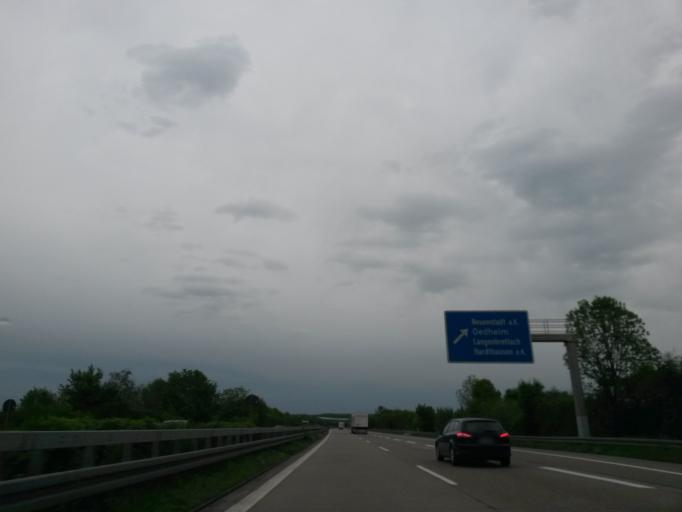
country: DE
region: Baden-Wuerttemberg
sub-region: Regierungsbezirk Stuttgart
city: Neuenstadt am Kocher
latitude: 49.2311
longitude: 9.3505
